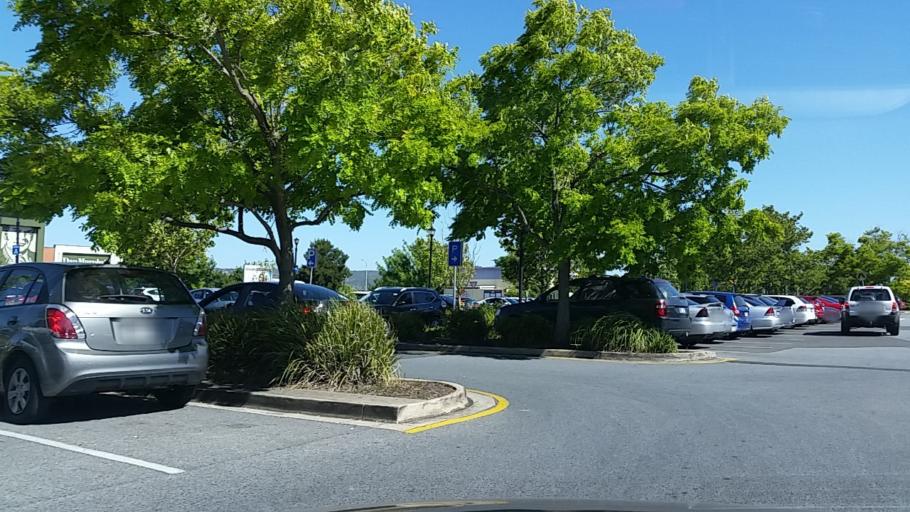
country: AU
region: South Australia
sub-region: Tea Tree Gully
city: Golden Grove
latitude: -34.7896
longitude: 138.6954
